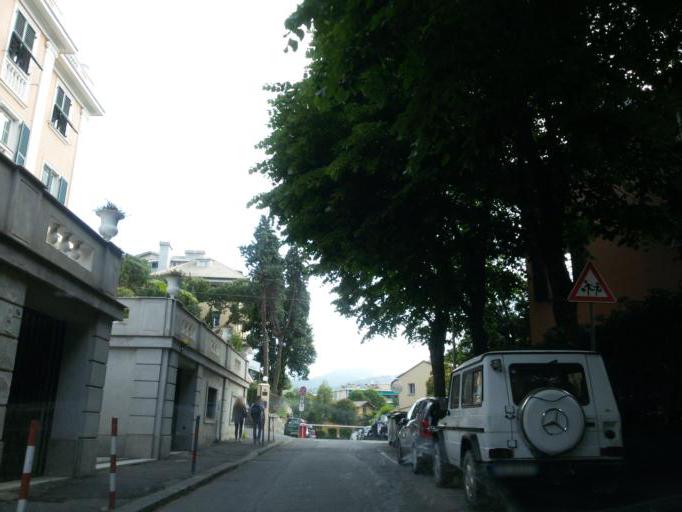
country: IT
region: Liguria
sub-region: Provincia di Genova
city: Genoa
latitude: 44.4018
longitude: 8.9604
